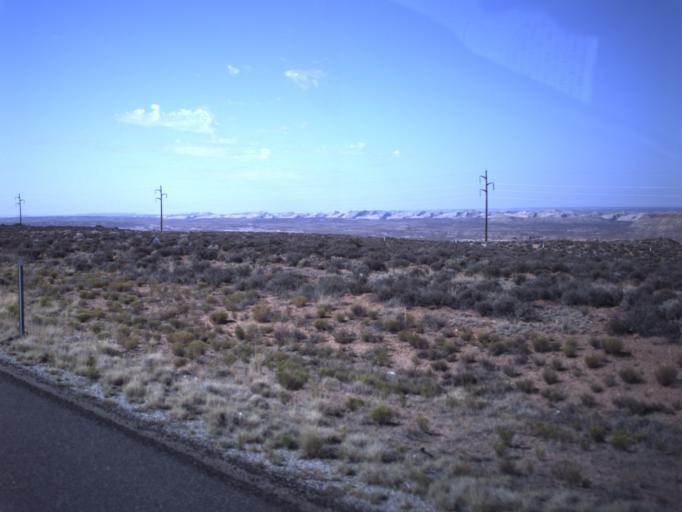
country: US
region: Utah
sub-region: San Juan County
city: Blanding
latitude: 37.3904
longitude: -109.4996
